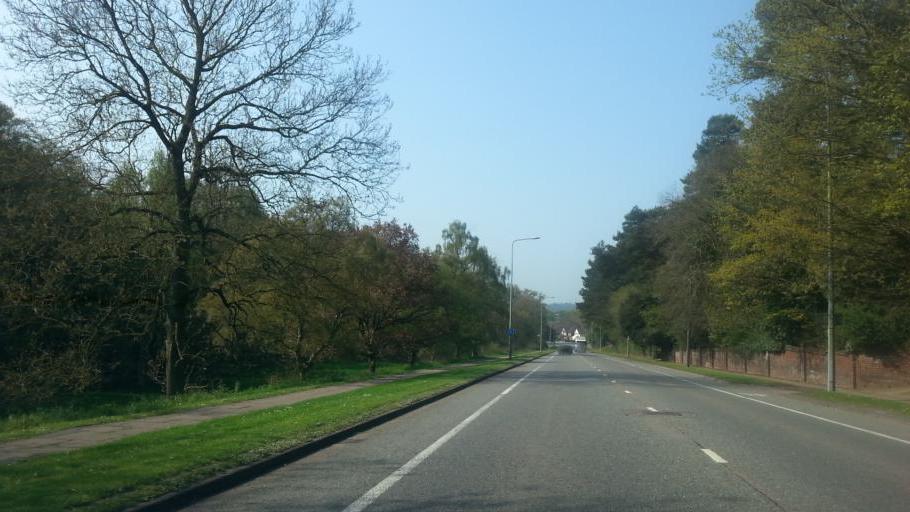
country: GB
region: England
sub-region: Suffolk
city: Ipswich
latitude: 52.0695
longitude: 1.1477
